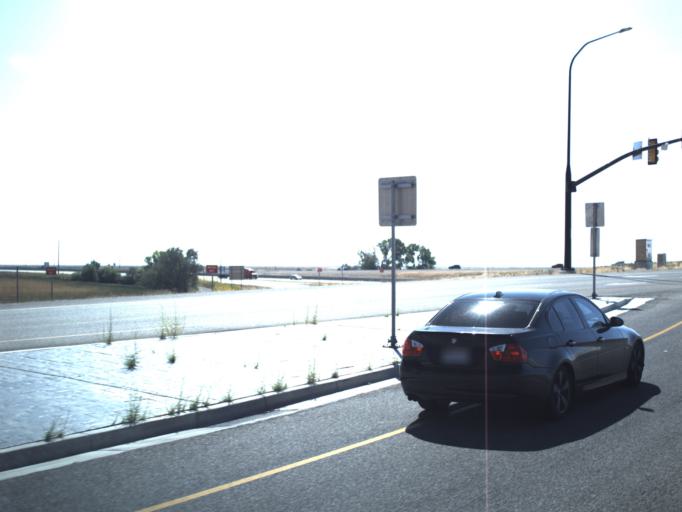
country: US
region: Utah
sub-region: Box Elder County
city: Perry
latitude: 41.4859
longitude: -112.0507
